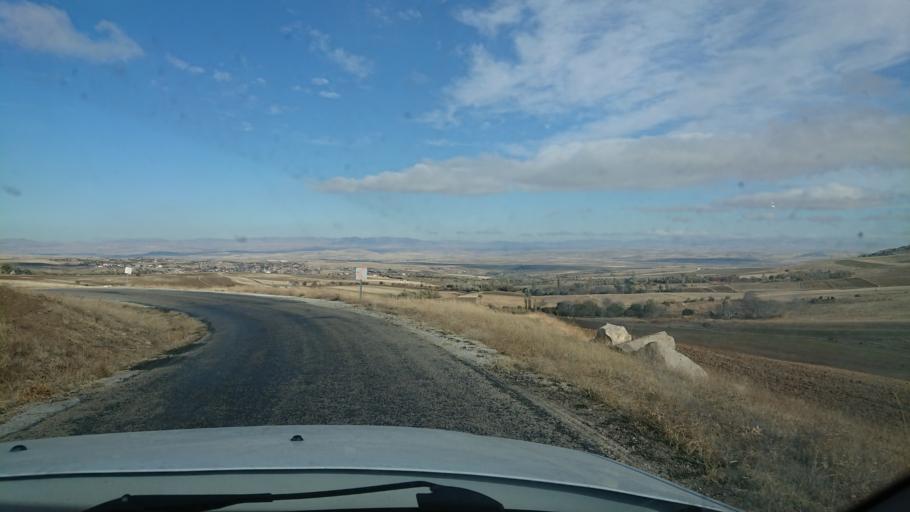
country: TR
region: Aksaray
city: Agacoren
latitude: 38.8429
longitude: 33.9528
